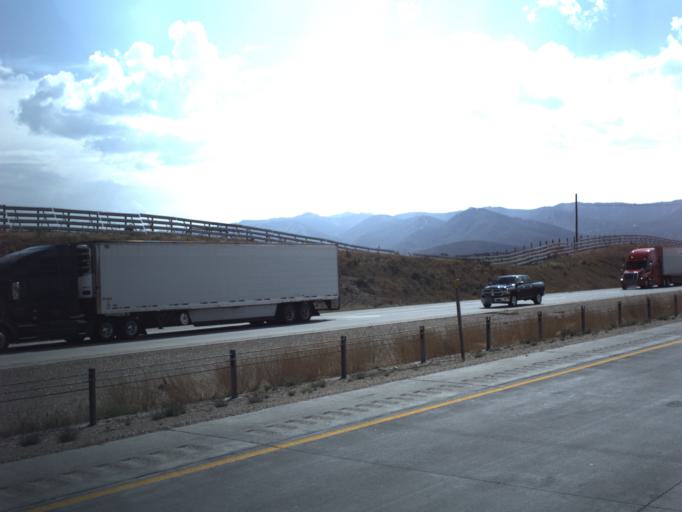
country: US
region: Utah
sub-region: Summit County
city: Snyderville
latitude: 40.7391
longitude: -111.4816
